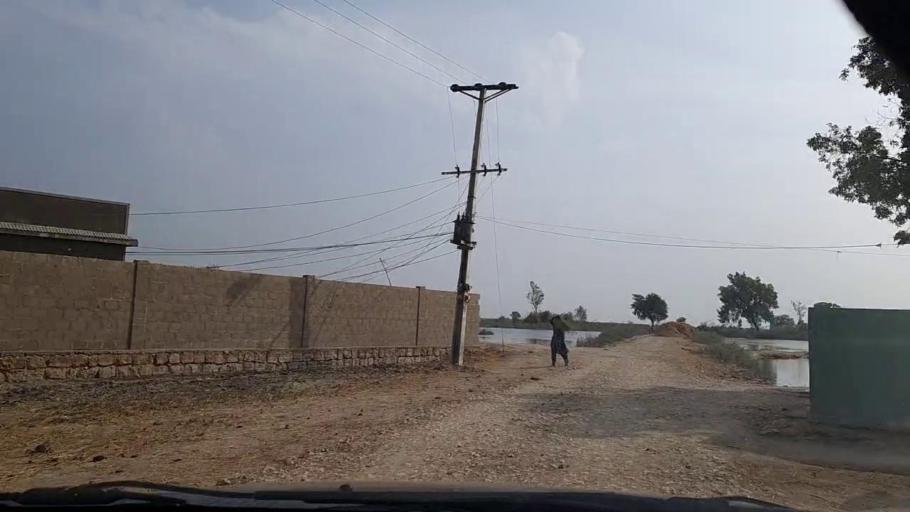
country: PK
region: Sindh
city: Thatta
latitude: 24.5822
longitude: 67.9032
